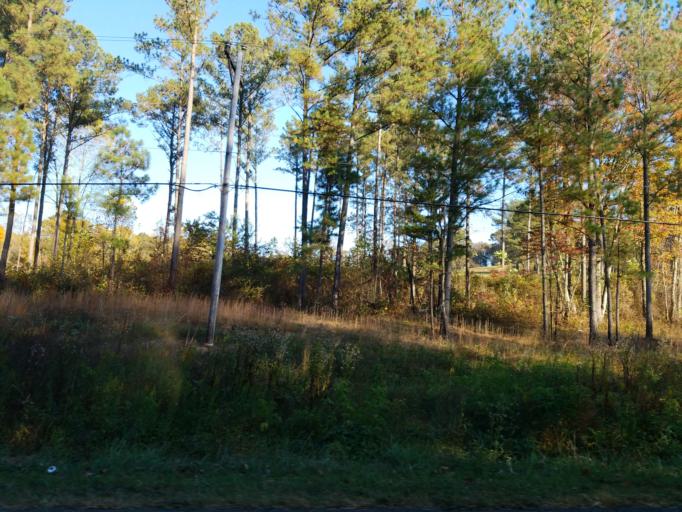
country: US
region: Georgia
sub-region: Gilmer County
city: Ellijay
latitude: 34.6076
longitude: -84.3962
